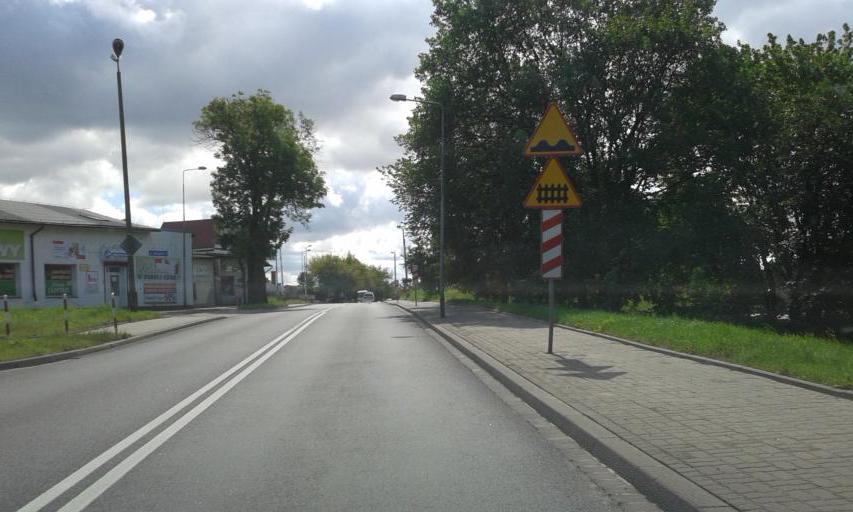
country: PL
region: West Pomeranian Voivodeship
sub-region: Powiat walecki
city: Walcz
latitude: 53.2684
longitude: 16.4851
